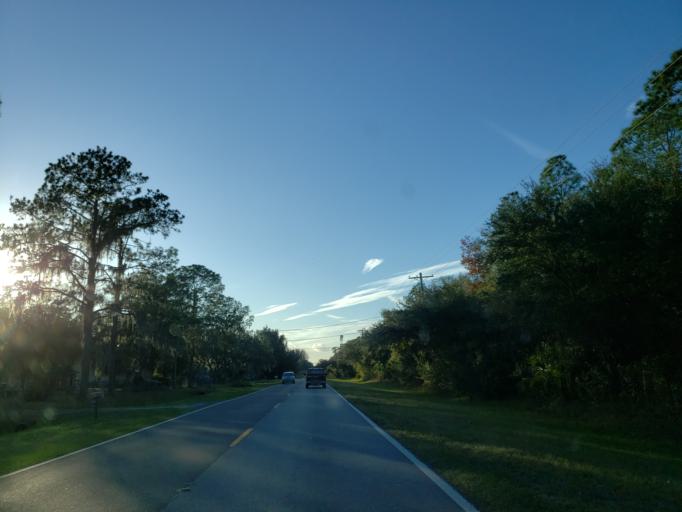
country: US
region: Florida
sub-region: Hillsborough County
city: Boyette
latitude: 27.8215
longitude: -82.2814
